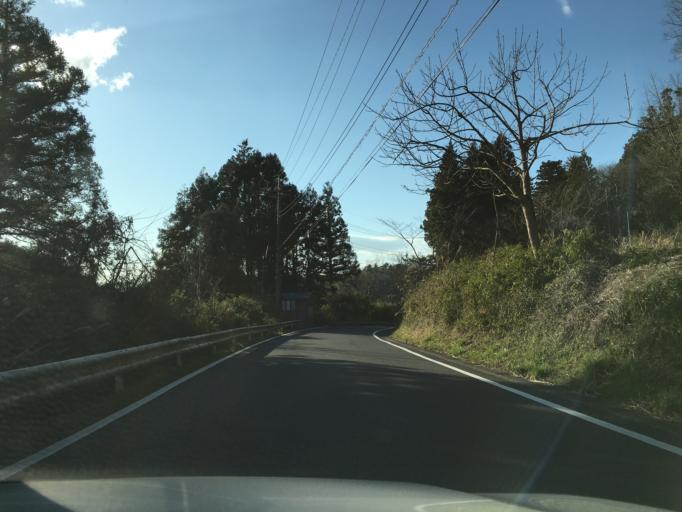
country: JP
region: Ibaraki
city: Daigo
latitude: 36.7735
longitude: 140.2502
